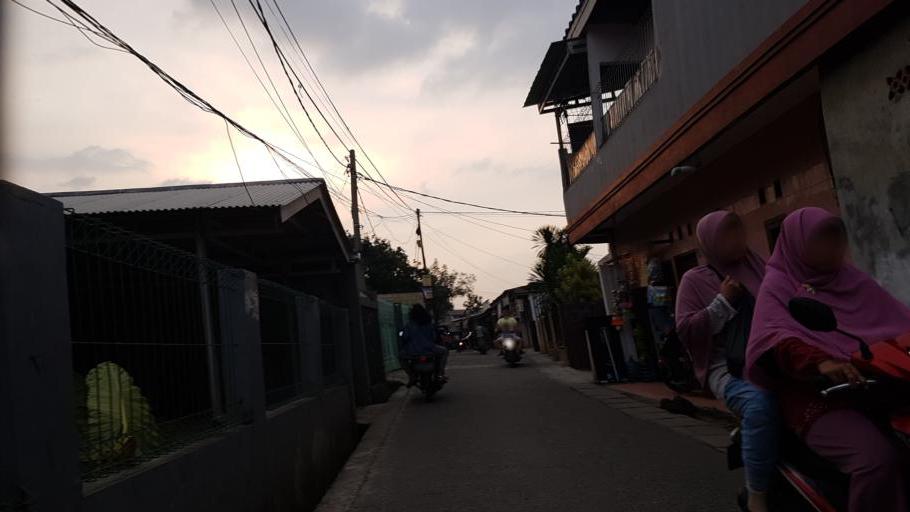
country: ID
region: West Java
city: Depok
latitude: -6.3819
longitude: 106.8040
